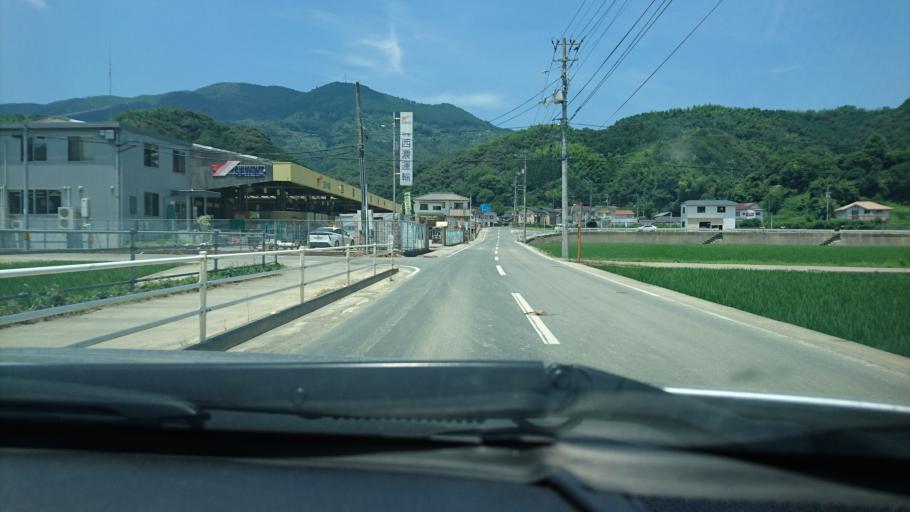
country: JP
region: Ehime
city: Ozu
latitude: 33.5074
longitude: 132.5291
